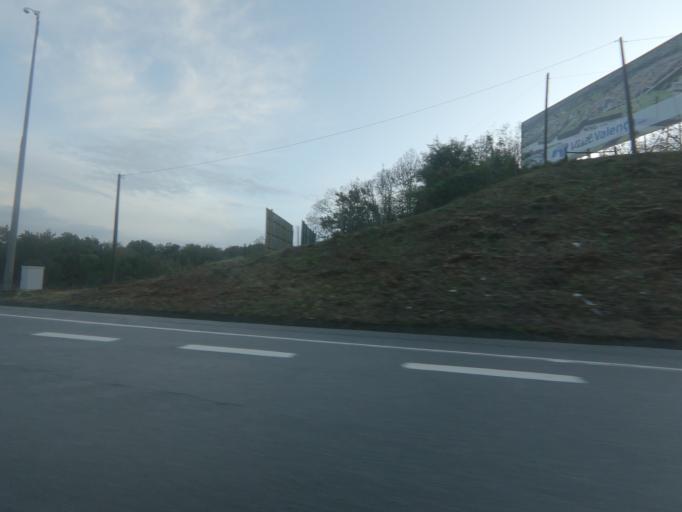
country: PT
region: Viana do Castelo
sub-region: Valenca
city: Valenca
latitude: 42.0292
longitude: -8.6508
